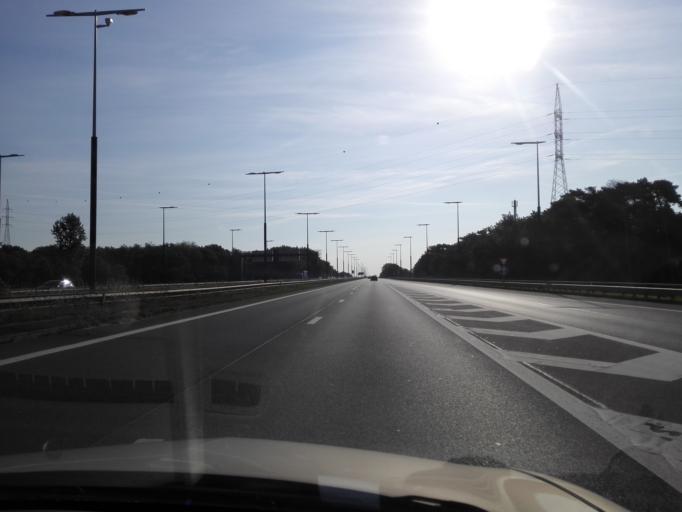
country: BE
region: Flanders
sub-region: Provincie Limburg
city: Lummen
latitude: 51.0002
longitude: 5.2325
